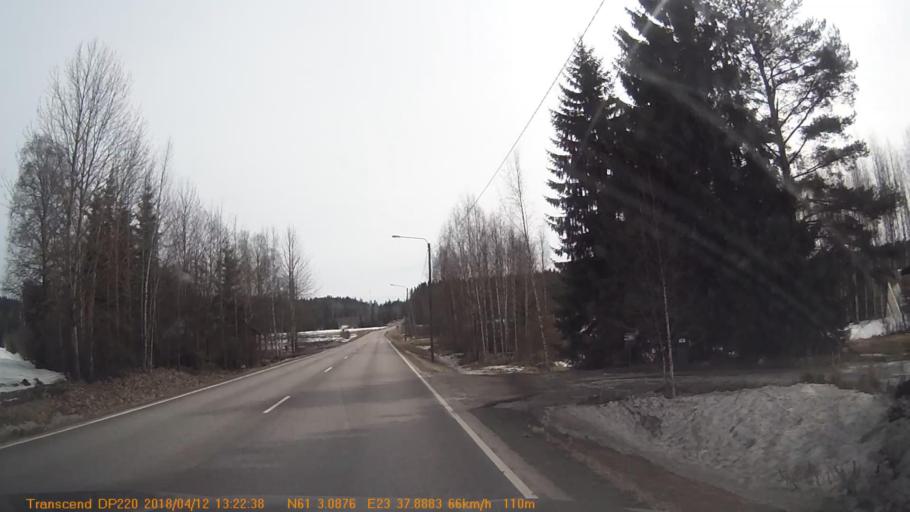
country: FI
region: Pirkanmaa
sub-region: Etelae-Pirkanmaa
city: Urjala
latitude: 61.0505
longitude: 23.6326
